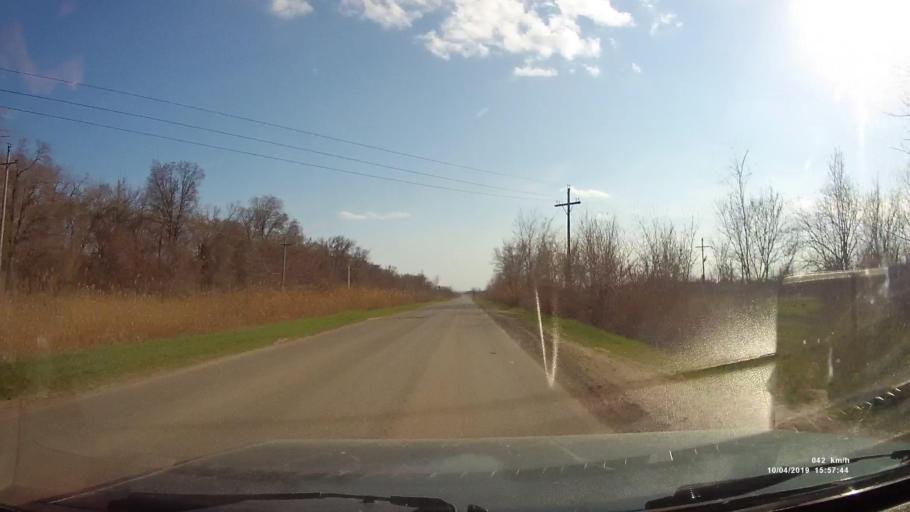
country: RU
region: Rostov
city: Masalovka
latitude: 48.4088
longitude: 40.2750
